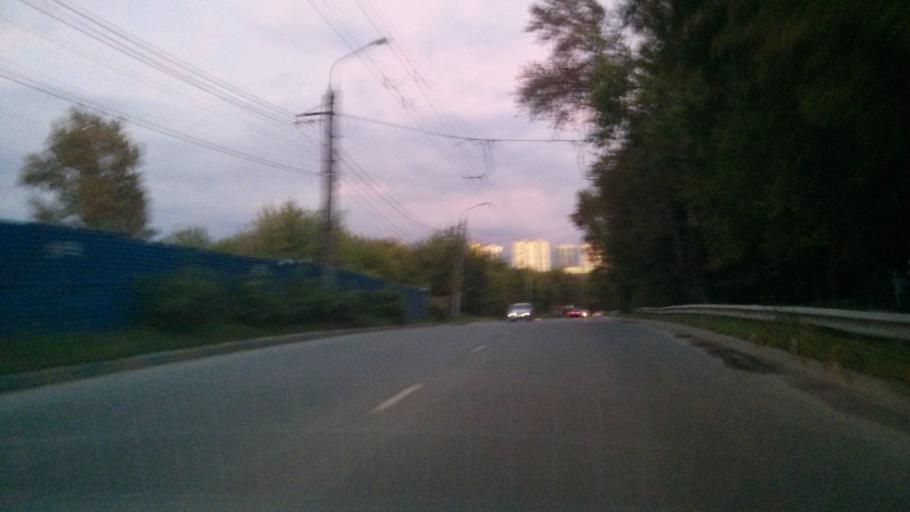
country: RU
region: Nizjnij Novgorod
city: Afonino
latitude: 56.2947
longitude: 44.0530
